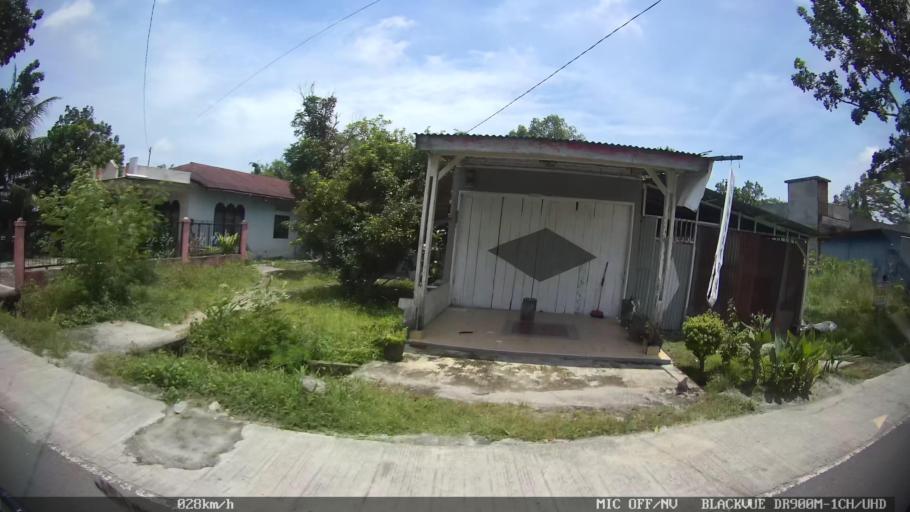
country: ID
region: North Sumatra
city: Percut
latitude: 3.5585
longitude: 98.8617
